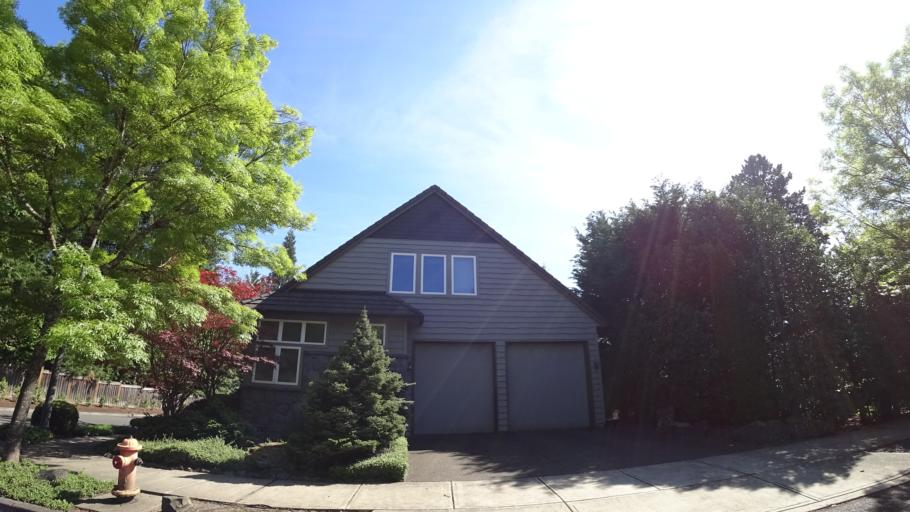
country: US
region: Oregon
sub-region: Washington County
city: Raleigh Hills
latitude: 45.4919
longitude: -122.7429
